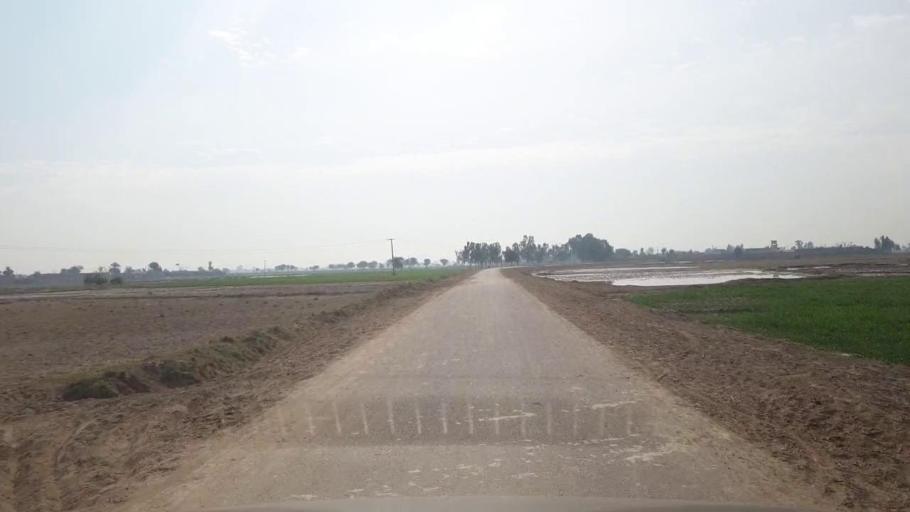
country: PK
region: Sindh
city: Hala
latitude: 25.9915
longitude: 68.4219
